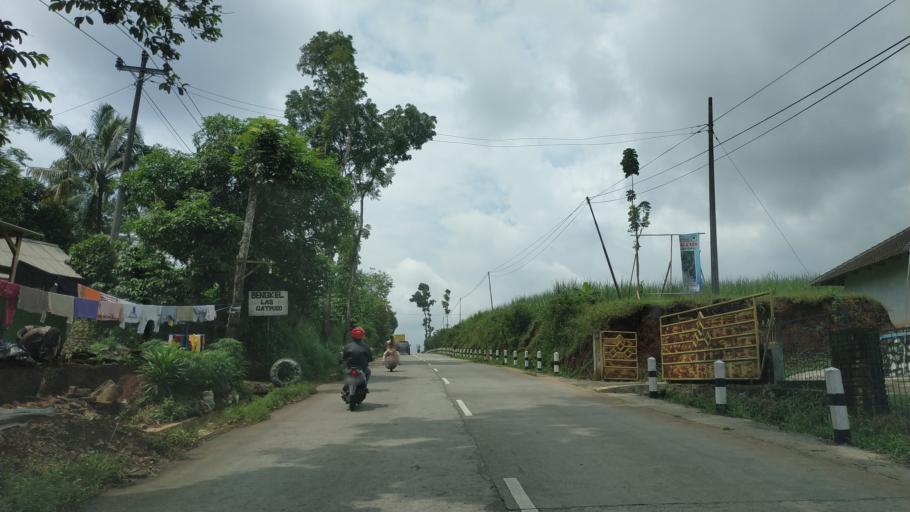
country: ID
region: Central Java
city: Weleri
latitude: -7.1011
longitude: 110.0663
